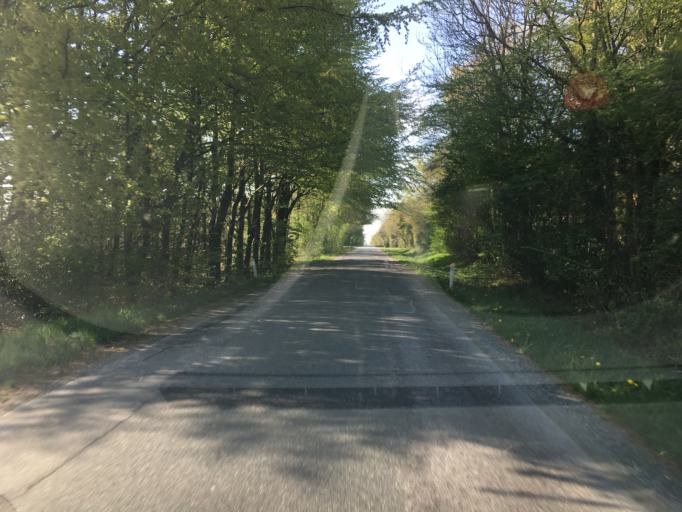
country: DK
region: South Denmark
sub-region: Haderslev Kommune
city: Vojens
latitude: 55.2395
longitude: 9.3230
